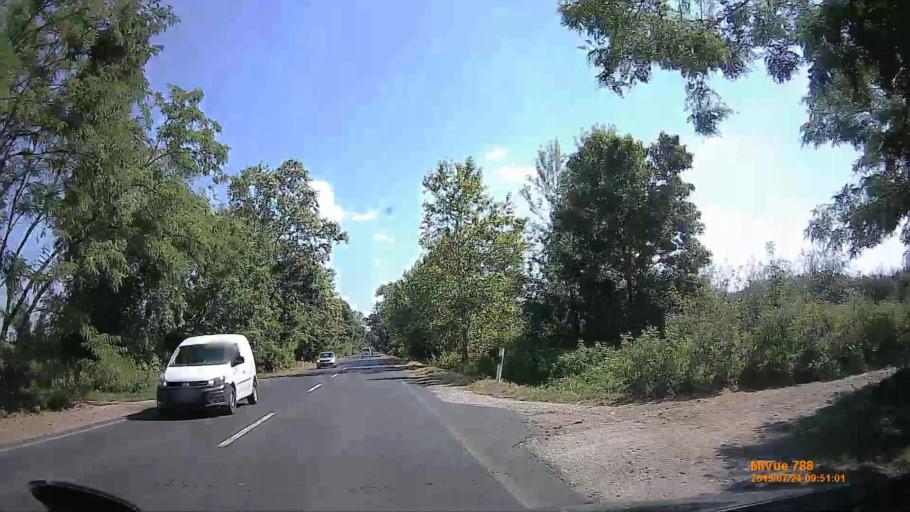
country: HU
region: Szabolcs-Szatmar-Bereg
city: Vaja
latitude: 48.0270
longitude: 22.1614
